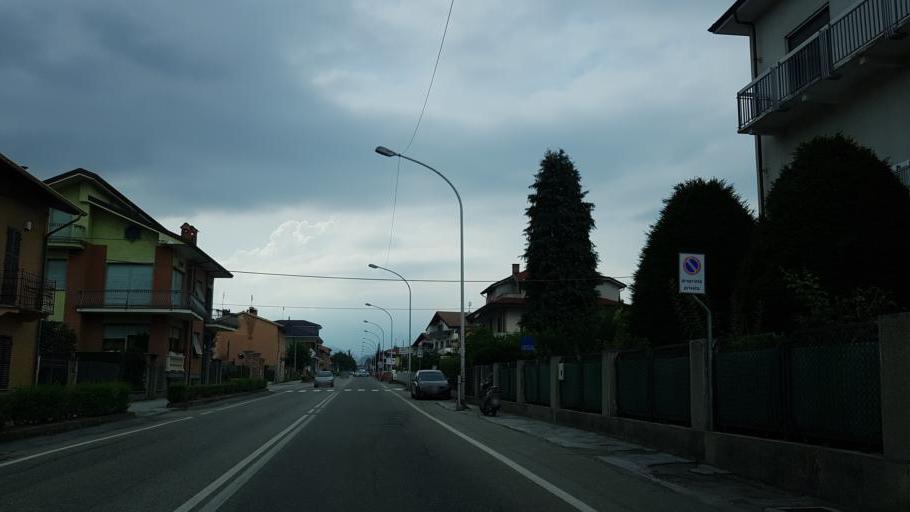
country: IT
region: Piedmont
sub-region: Provincia di Cuneo
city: Borgo San Dalmazzo
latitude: 44.3308
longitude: 7.4811
